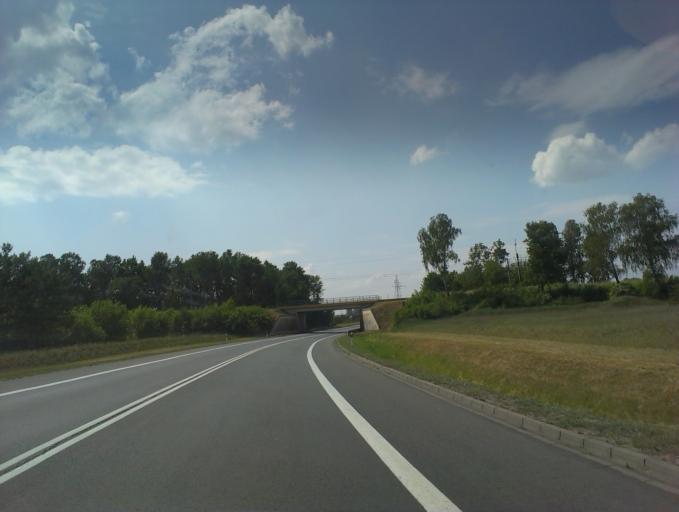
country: PL
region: Greater Poland Voivodeship
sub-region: Powiat pilski
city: Pila
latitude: 53.1381
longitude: 16.7861
